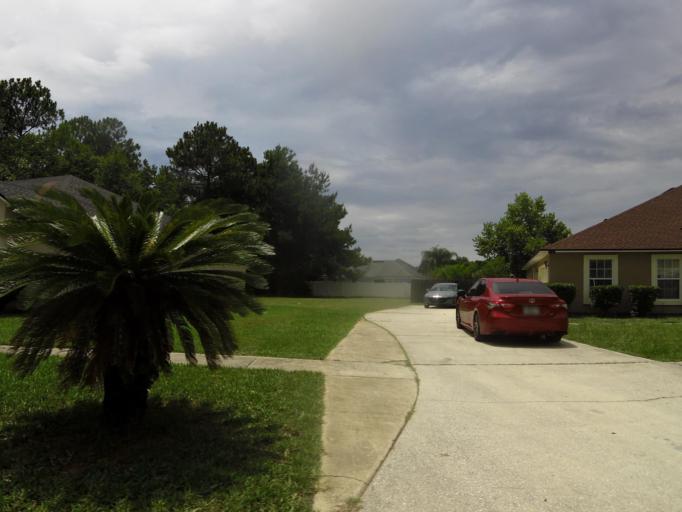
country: US
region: Florida
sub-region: Duval County
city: Jacksonville
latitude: 30.4249
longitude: -81.7257
